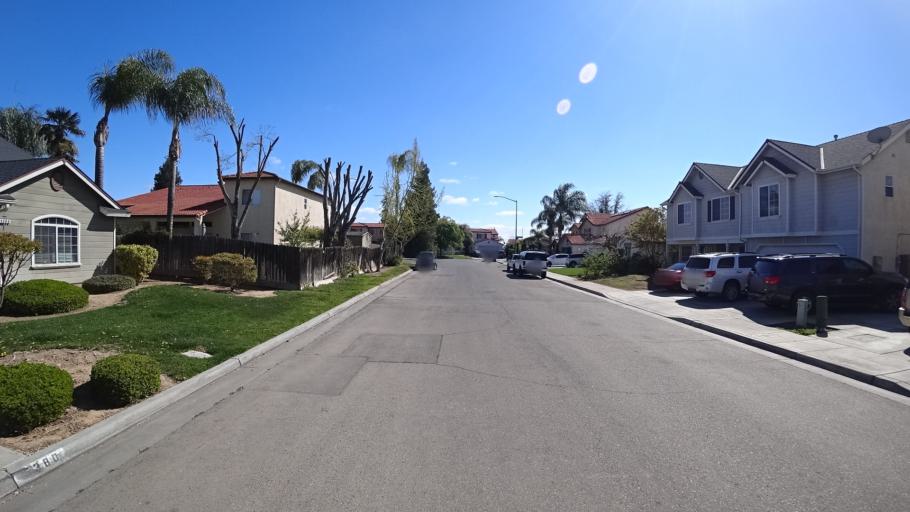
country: US
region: California
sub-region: Fresno County
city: West Park
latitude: 36.7897
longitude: -119.8874
